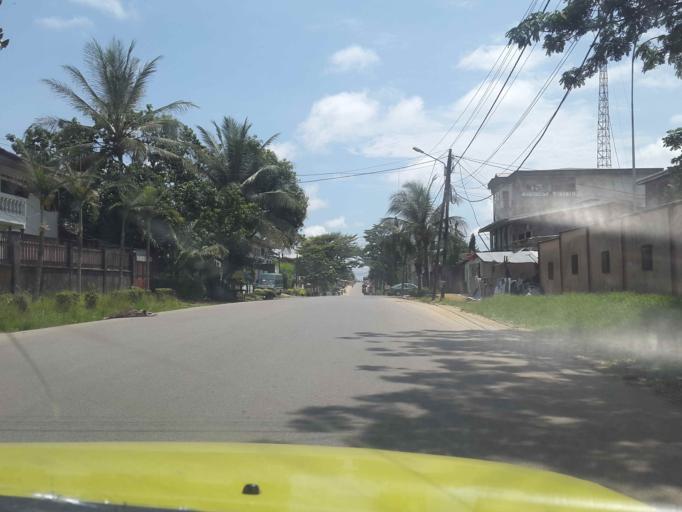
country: CM
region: Littoral
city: Douala
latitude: 4.0877
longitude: 9.7466
